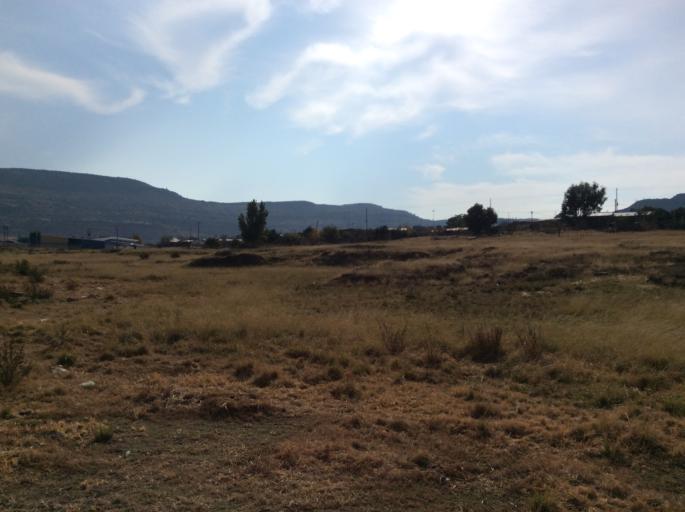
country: LS
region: Mafeteng
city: Mafeteng
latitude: -29.7242
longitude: 27.0253
